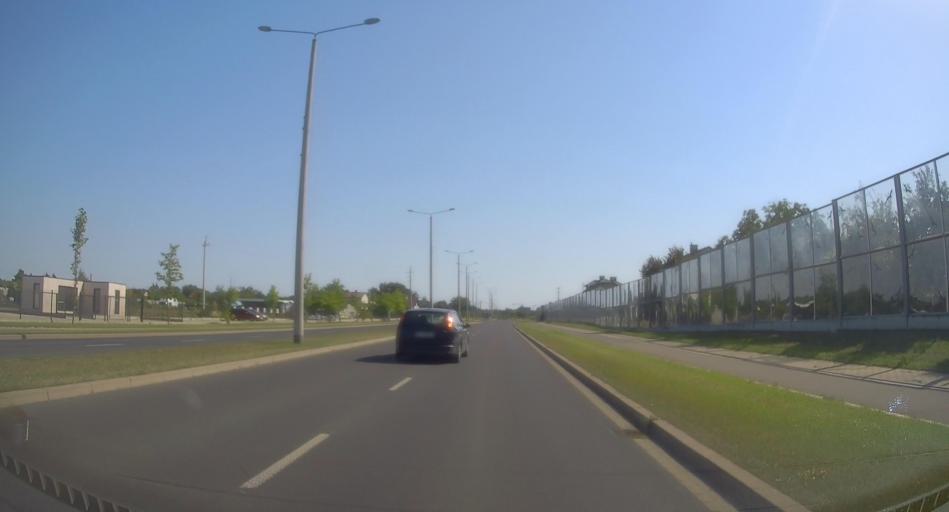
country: PL
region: Lodz Voivodeship
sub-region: Skierniewice
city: Skierniewice
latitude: 51.9501
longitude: 20.1591
